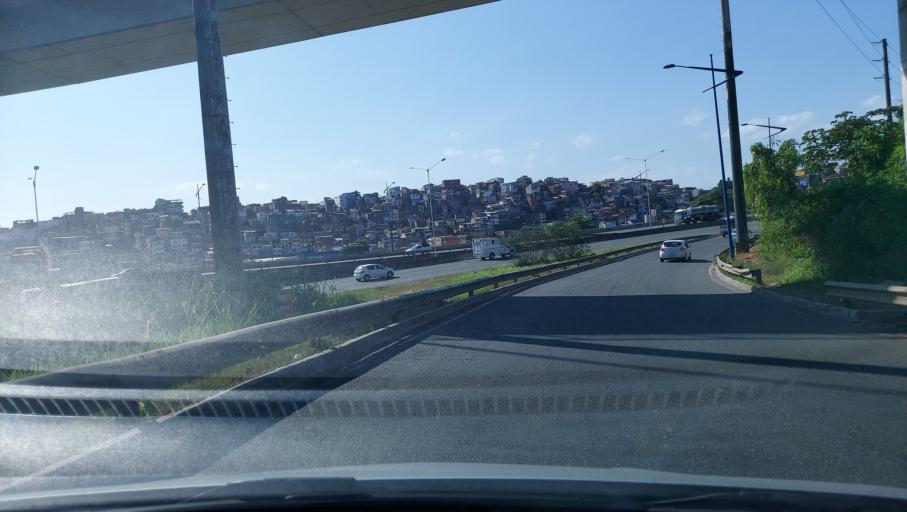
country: BR
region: Bahia
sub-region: Salvador
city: Salvador
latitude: -12.9657
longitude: -38.4765
